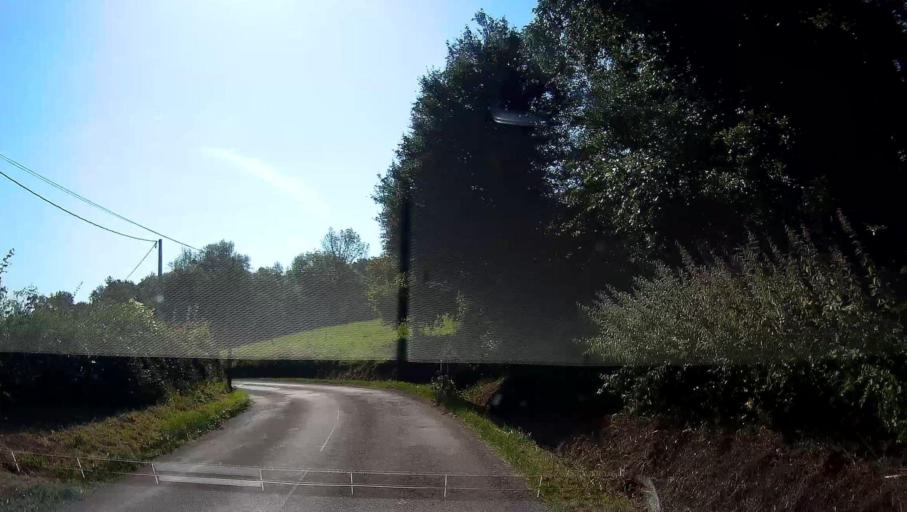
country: FR
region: Bourgogne
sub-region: Departement de Saone-et-Loire
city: Couches
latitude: 46.8868
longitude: 4.5712
